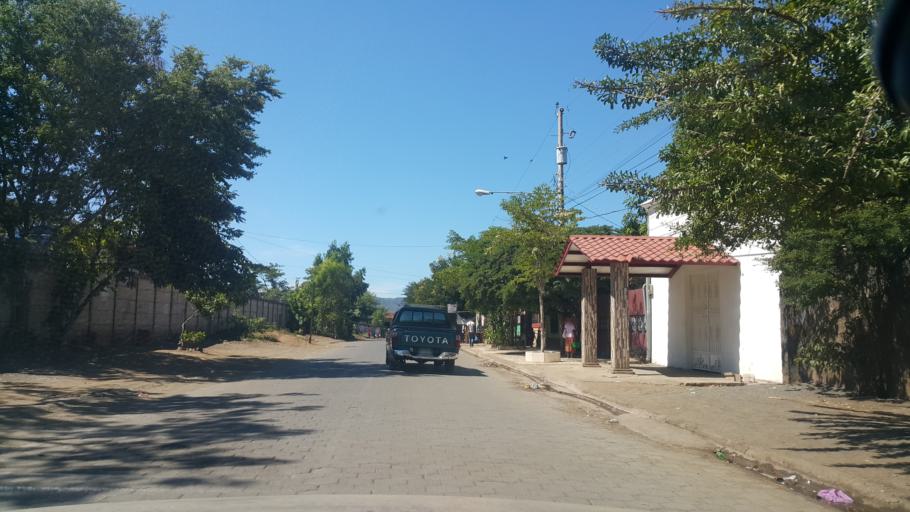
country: NI
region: Managua
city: Ciudad Sandino
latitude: 12.1479
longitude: -86.3492
